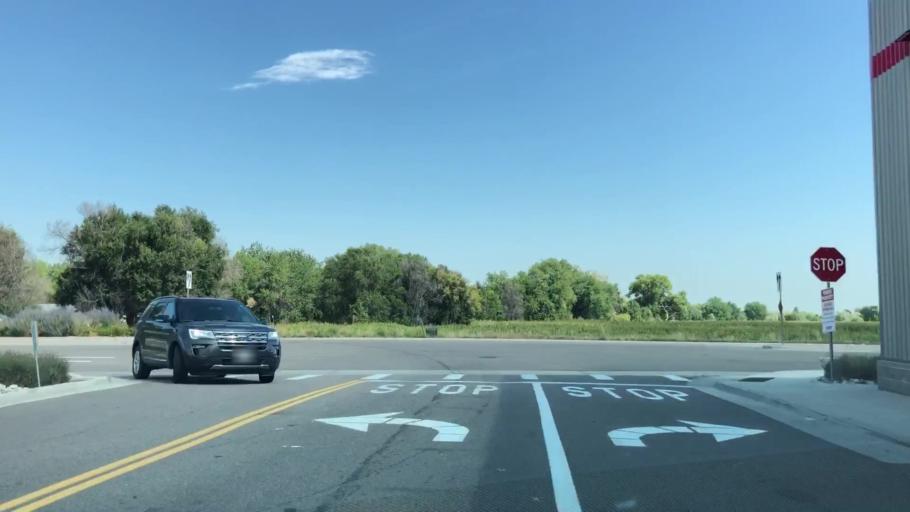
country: US
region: Colorado
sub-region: Weld County
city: Windsor
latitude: 40.5211
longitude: -104.9887
